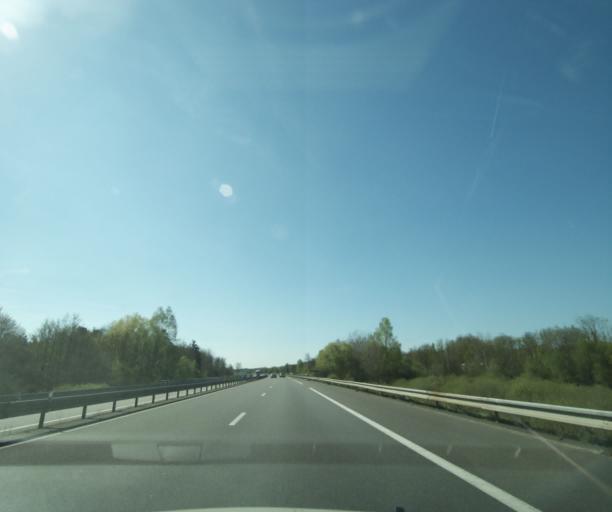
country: FR
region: Centre
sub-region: Departement du Loir-et-Cher
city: Theillay
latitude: 47.3409
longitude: 2.0477
